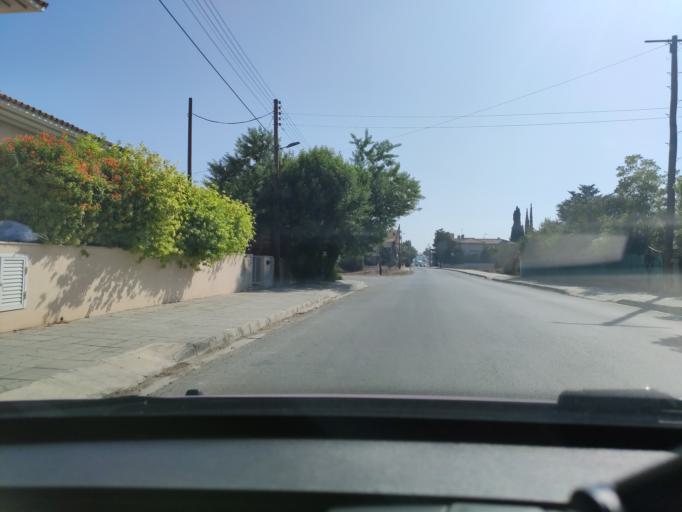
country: CY
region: Lefkosia
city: Nicosia
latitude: 35.1378
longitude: 33.3294
